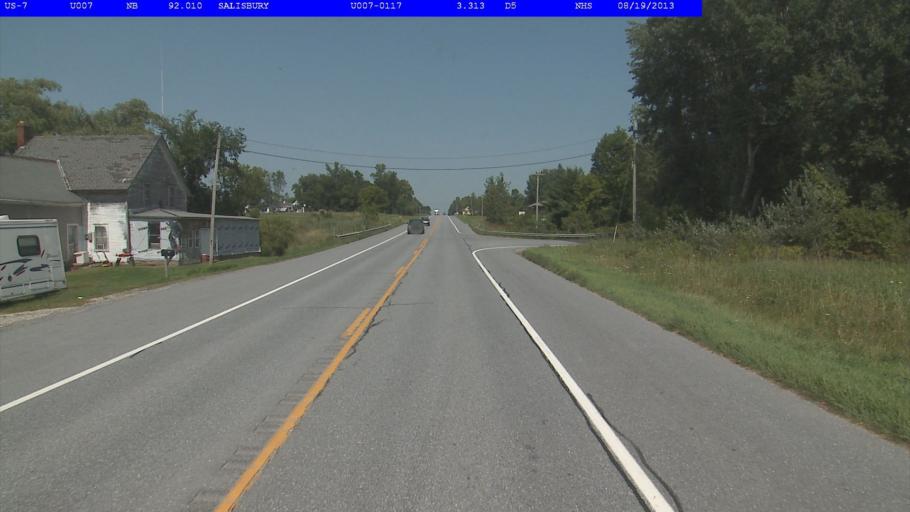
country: US
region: Vermont
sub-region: Addison County
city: Middlebury (village)
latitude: 43.9395
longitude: -73.1099
